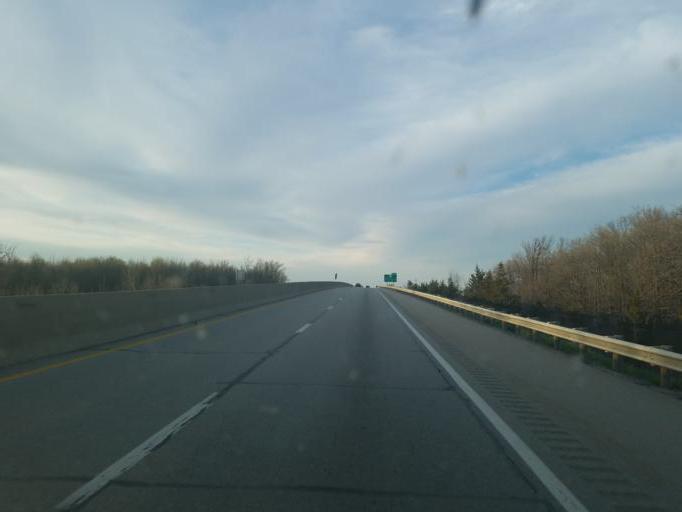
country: US
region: Ohio
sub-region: Wood County
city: Millbury
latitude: 41.5505
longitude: -83.4613
